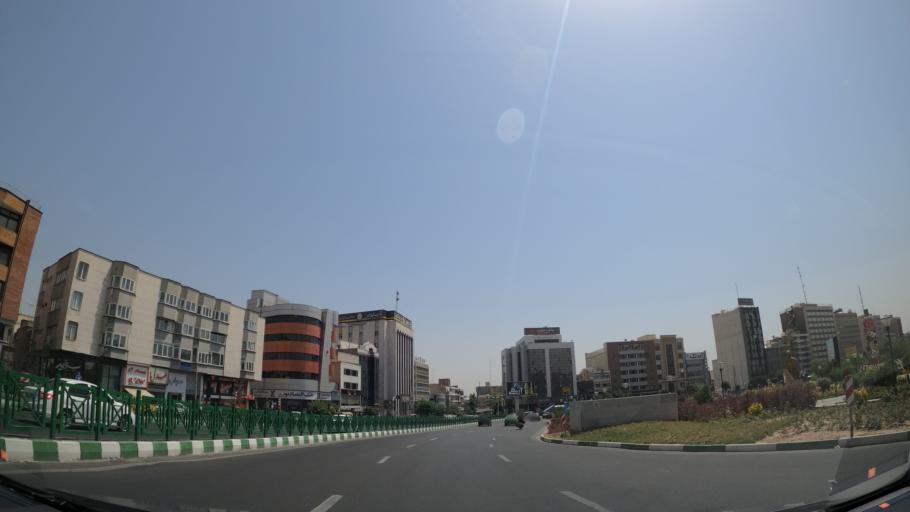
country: IR
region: Tehran
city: Tehran
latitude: 35.7165
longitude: 51.4264
